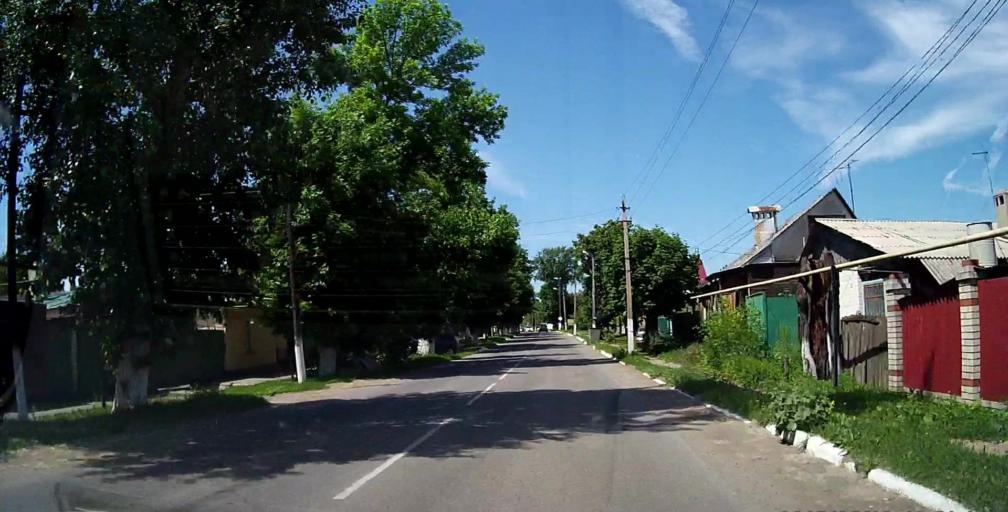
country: RU
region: Lipetsk
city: Chaplygin
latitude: 53.2430
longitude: 39.9721
